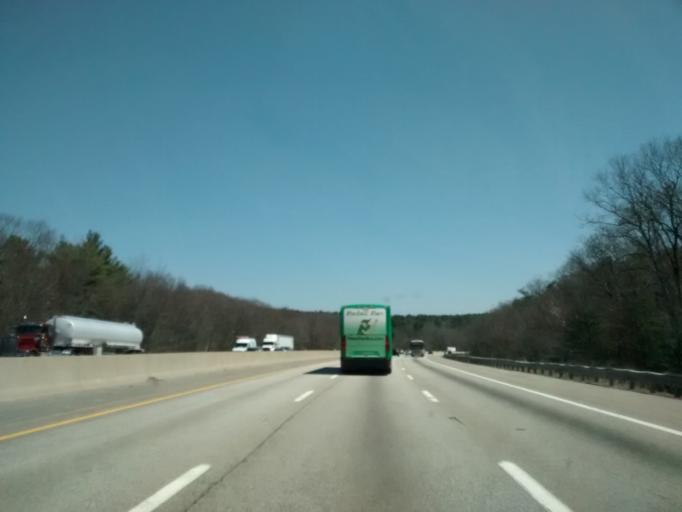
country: US
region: Massachusetts
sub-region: Worcester County
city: Grafton
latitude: 42.2283
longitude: -71.6603
